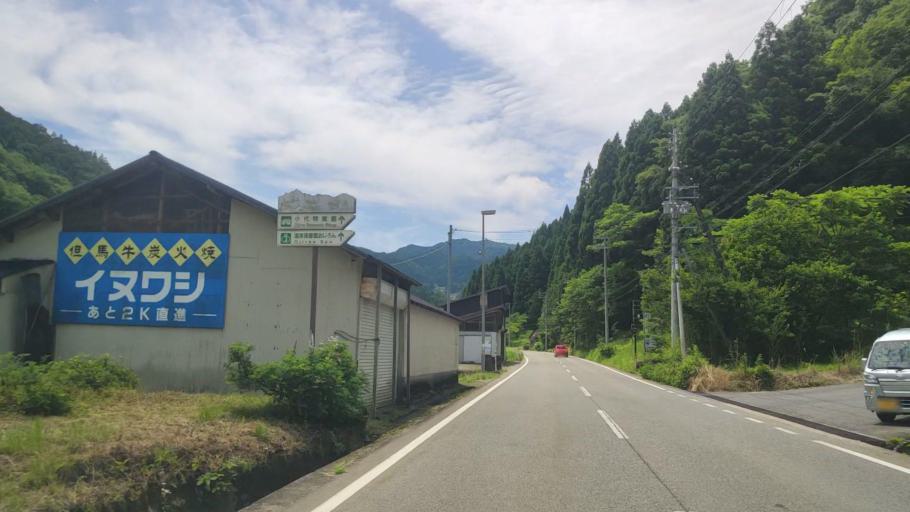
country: JP
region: Hyogo
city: Toyooka
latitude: 35.4762
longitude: 134.5520
